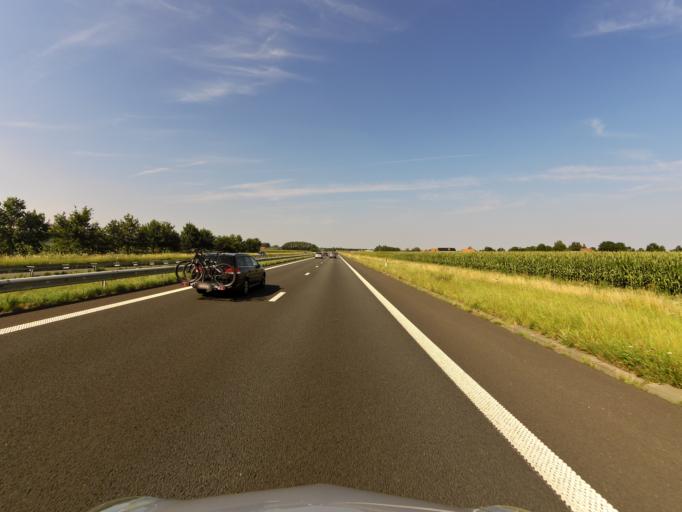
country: BE
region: Flanders
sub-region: Provincie West-Vlaanderen
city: Lichtervelde
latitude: 51.0461
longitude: 3.1620
